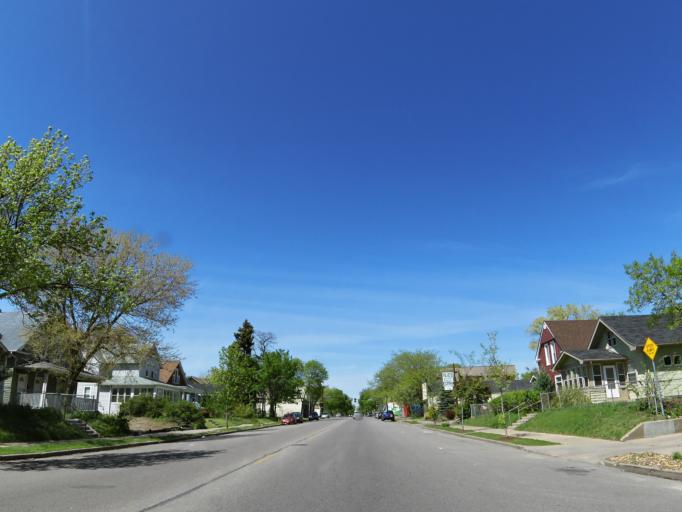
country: US
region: Minnesota
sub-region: Hennepin County
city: Minneapolis
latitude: 44.9380
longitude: -93.2625
